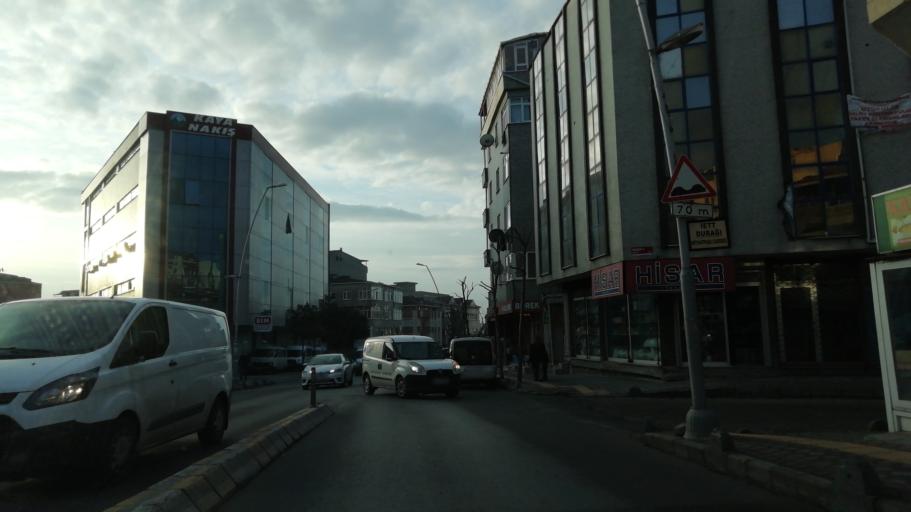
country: TR
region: Istanbul
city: Bahcelievler
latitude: 41.0097
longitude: 28.8272
